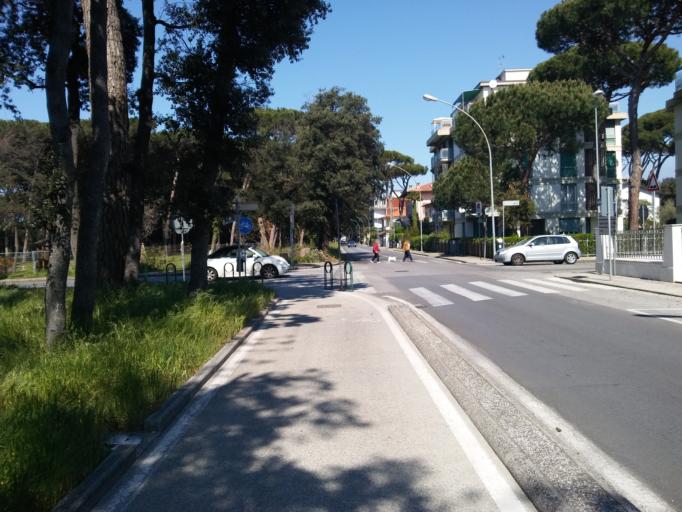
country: IT
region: Tuscany
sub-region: Provincia di Lucca
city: Viareggio
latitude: 43.8871
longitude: 10.2386
